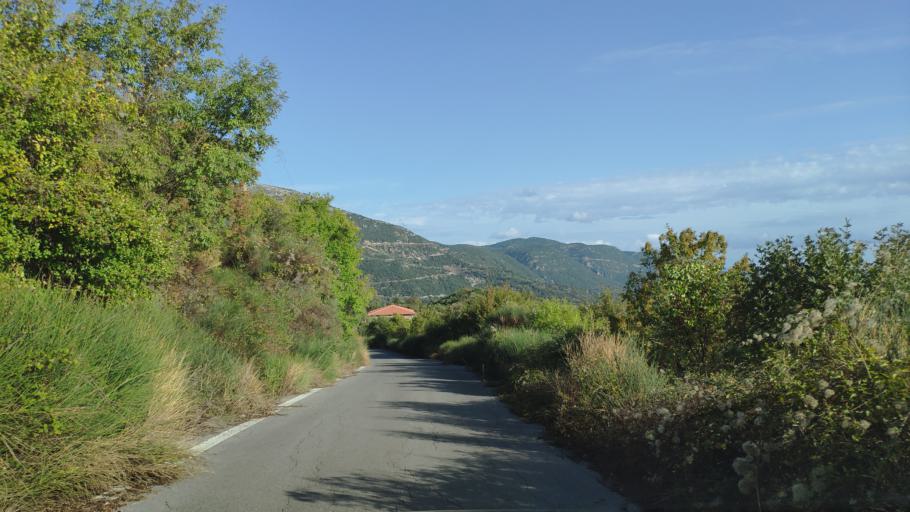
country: GR
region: Peloponnese
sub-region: Nomos Arkadias
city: Dimitsana
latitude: 37.5603
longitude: 22.0329
